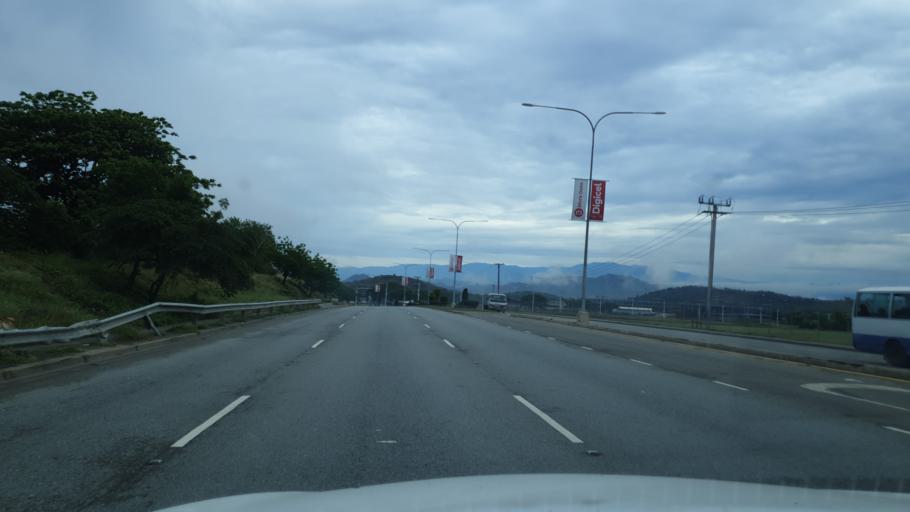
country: PG
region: National Capital
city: Port Moresby
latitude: -9.4306
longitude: 147.1793
